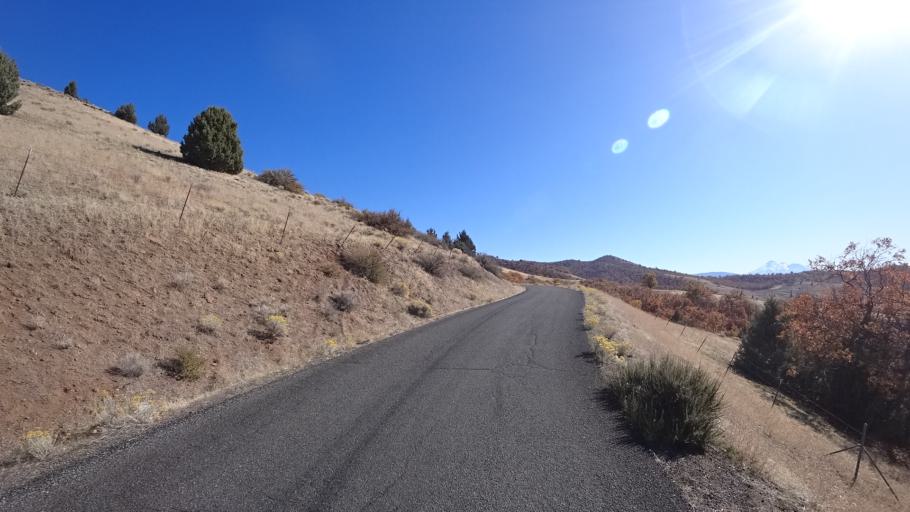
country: US
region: California
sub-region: Siskiyou County
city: Montague
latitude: 41.8241
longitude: -122.3402
